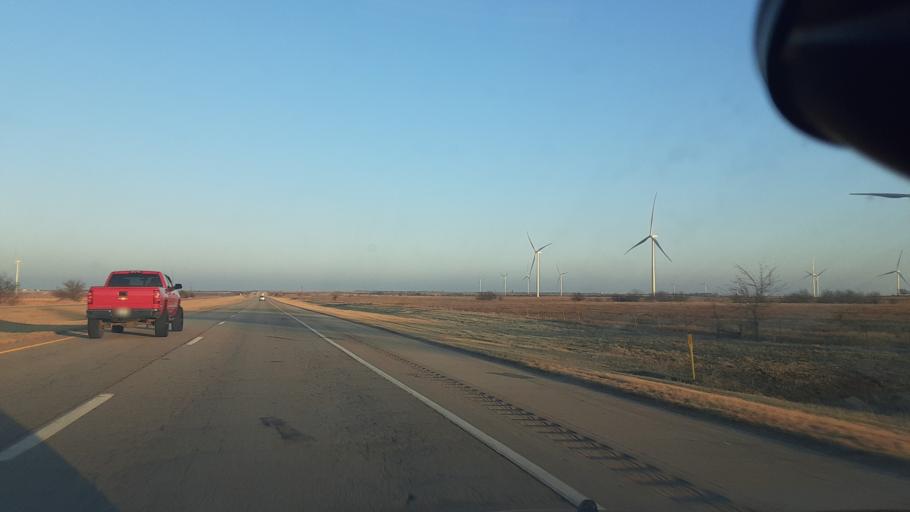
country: US
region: Oklahoma
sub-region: Noble County
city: Perry
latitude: 36.3979
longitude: -97.4167
